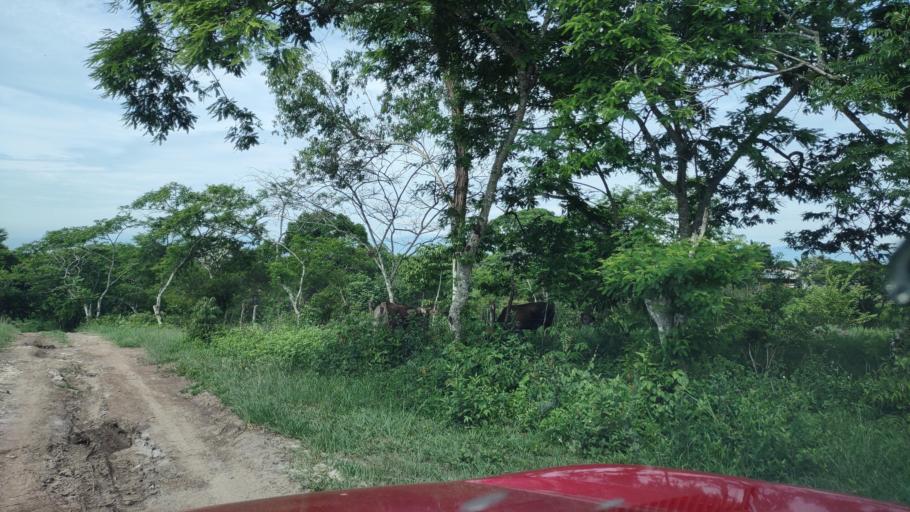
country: MX
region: Veracruz
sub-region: Emiliano Zapata
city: Dos Rios
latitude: 19.4687
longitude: -96.8273
